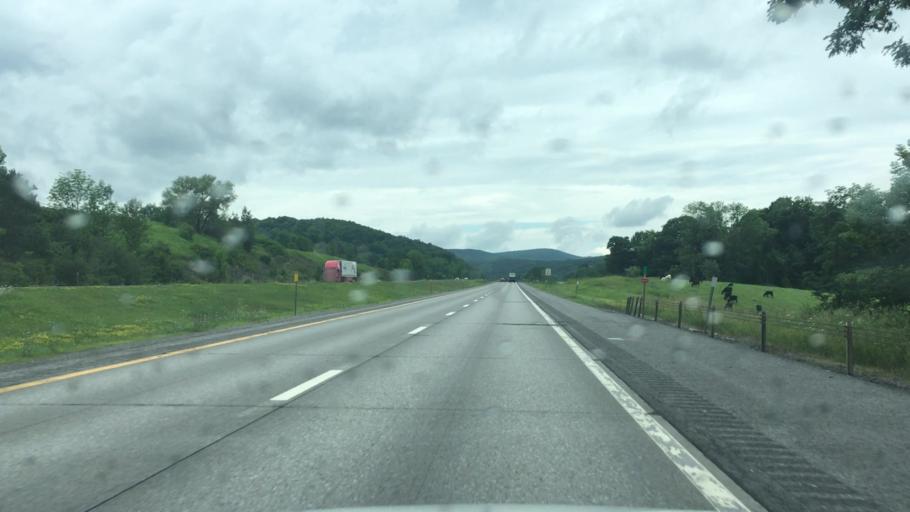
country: US
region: New York
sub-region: Schoharie County
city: Cobleskill
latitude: 42.6419
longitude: -74.5813
